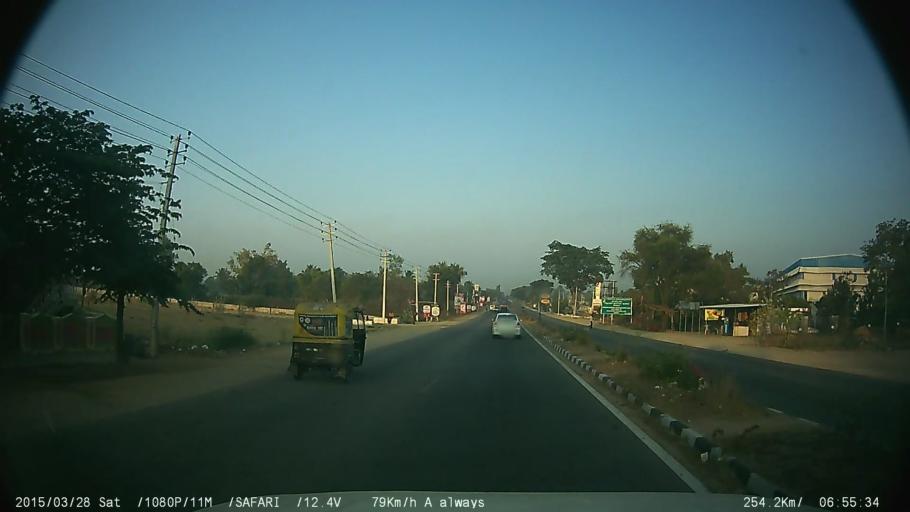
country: IN
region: Karnataka
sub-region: Mandya
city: Maddur
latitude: 12.5738
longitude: 77.0149
